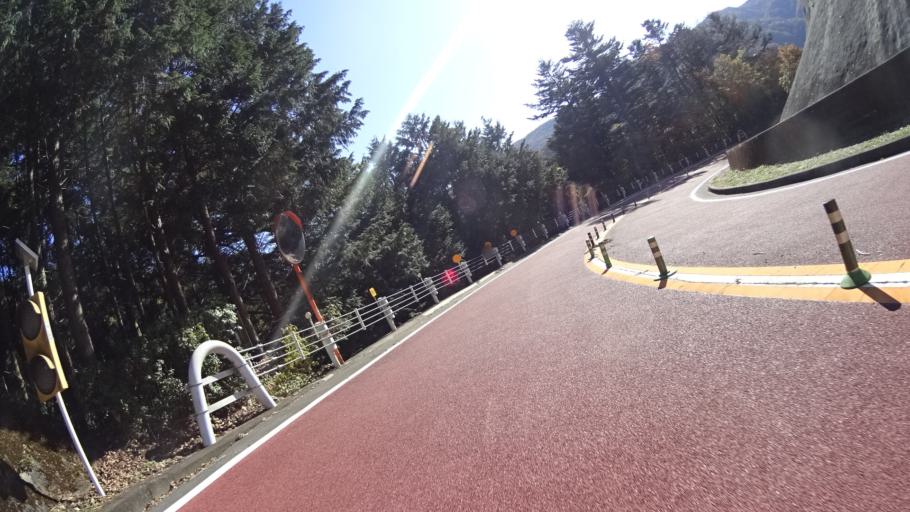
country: JP
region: Yamanashi
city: Uenohara
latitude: 35.7301
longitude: 139.0438
